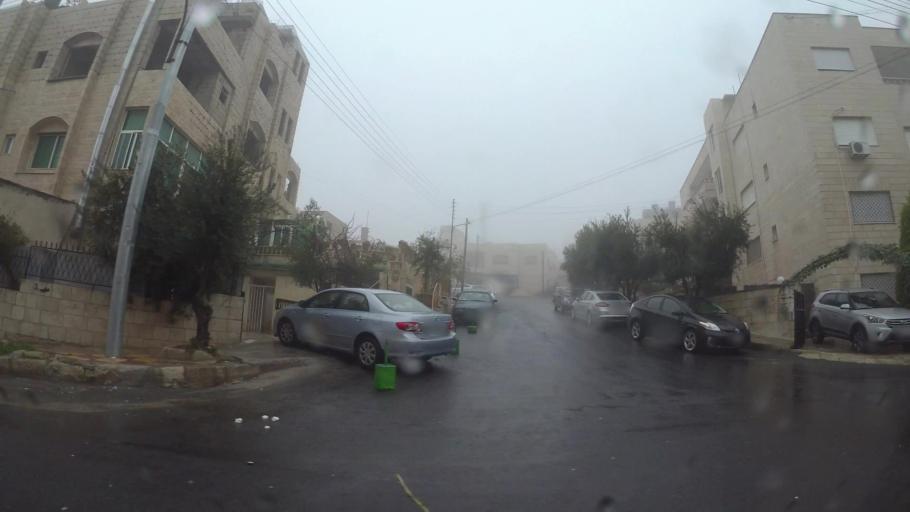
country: JO
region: Amman
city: Al Jubayhah
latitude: 32.0141
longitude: 35.8772
